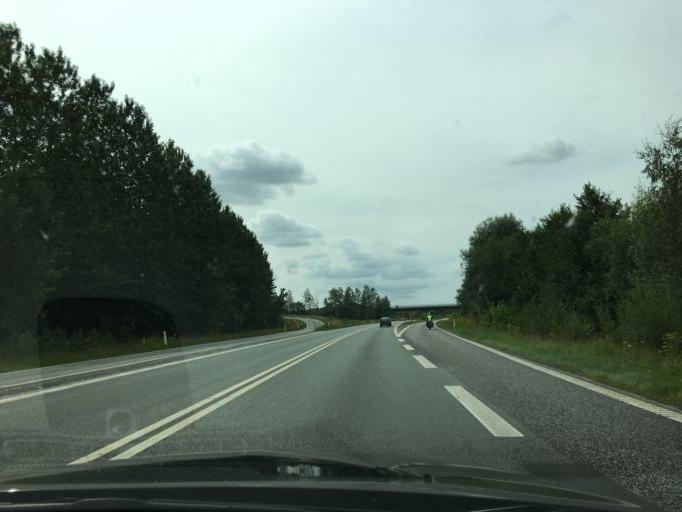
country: DK
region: Capital Region
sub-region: Hillerod Kommune
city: Hillerod
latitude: 55.9579
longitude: 12.2466
